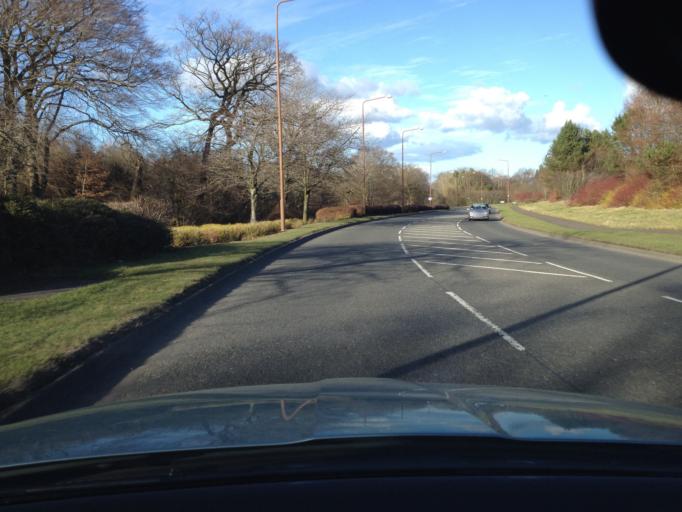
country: GB
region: Scotland
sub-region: West Lothian
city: Livingston
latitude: 55.8772
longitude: -3.5423
